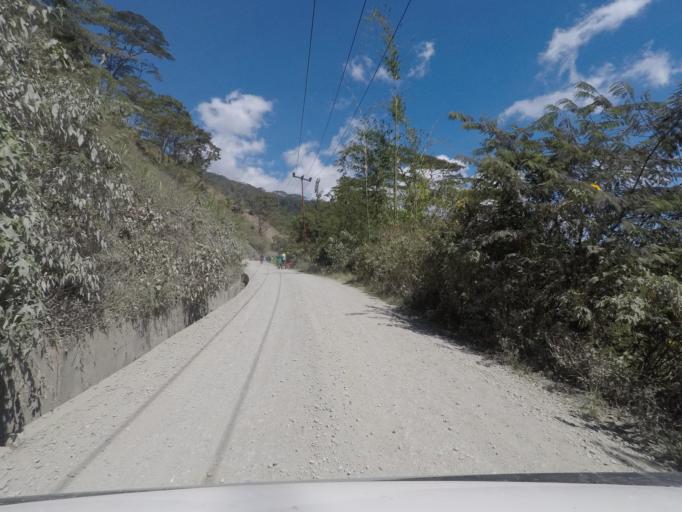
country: TL
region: Ermera
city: Gleno
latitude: -8.7455
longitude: 125.3911
